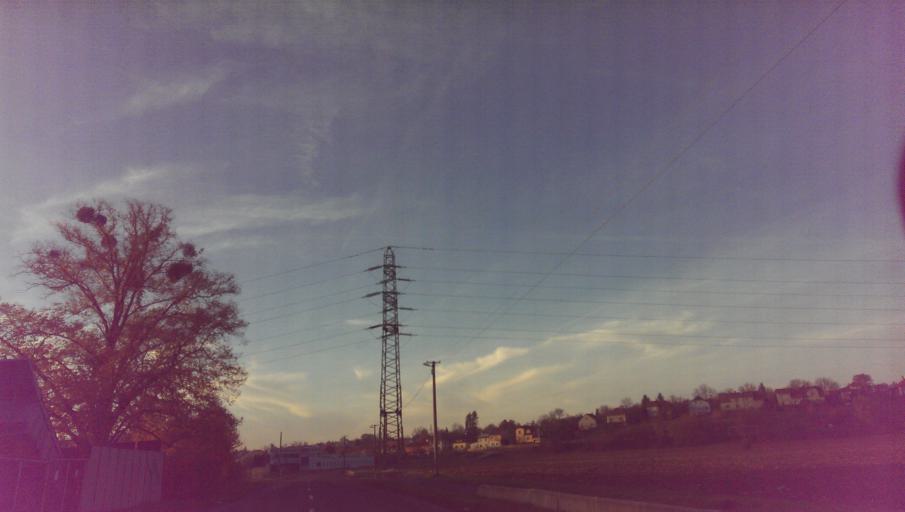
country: CZ
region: Zlin
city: Tecovice
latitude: 49.2144
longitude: 17.5945
